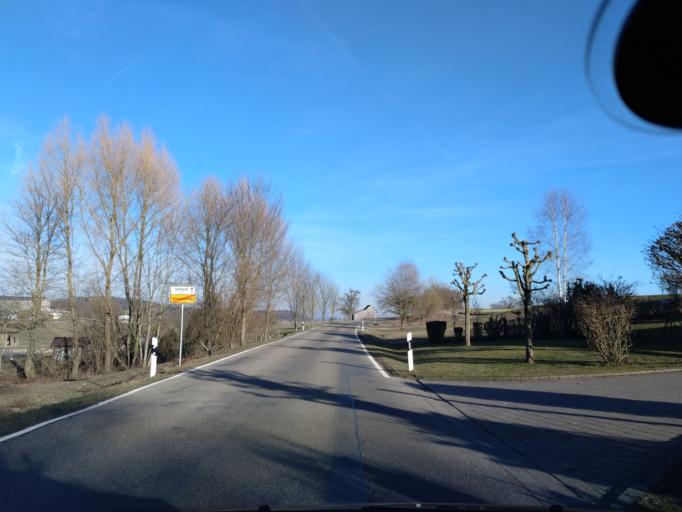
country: DE
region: Baden-Wuerttemberg
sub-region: Regierungsbezirk Stuttgart
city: Rosenberg
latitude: 49.0722
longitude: 9.9838
